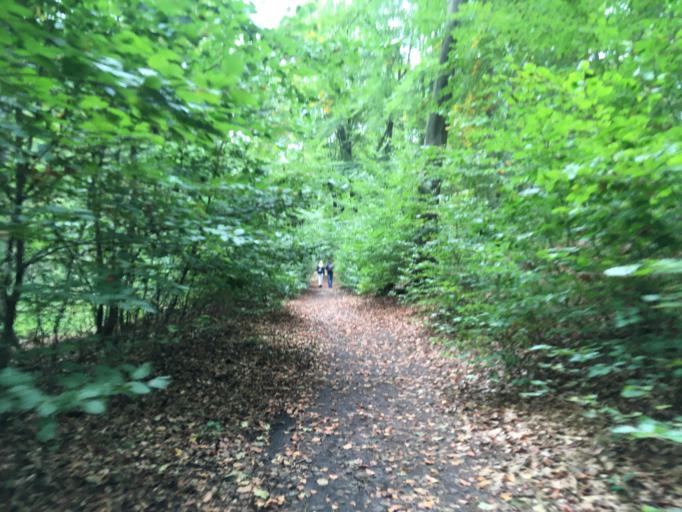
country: DE
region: Brandenburg
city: Birkenwerder
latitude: 52.7039
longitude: 13.3115
